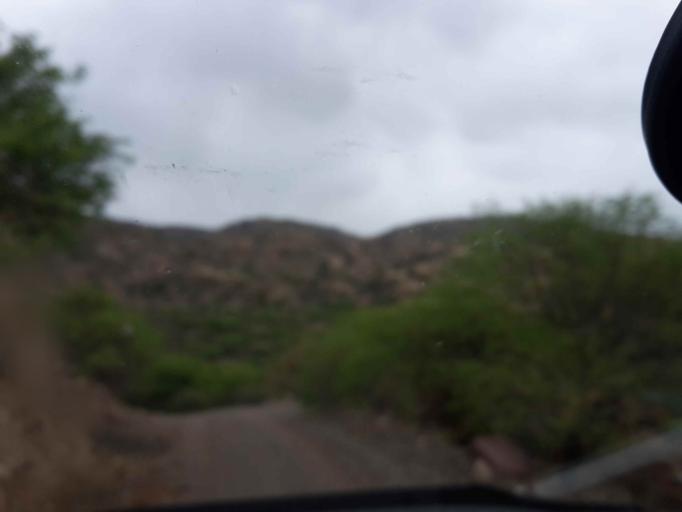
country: BO
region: Cochabamba
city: Sipe Sipe
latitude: -17.5297
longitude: -66.5203
